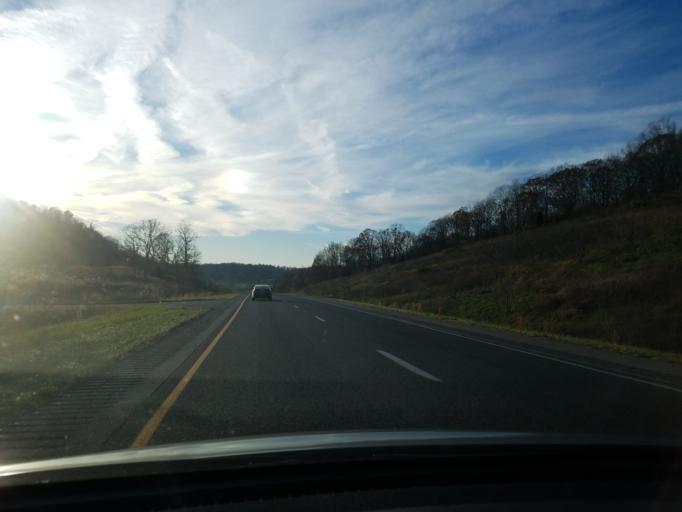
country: US
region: Indiana
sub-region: Dubois County
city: Ferdinand
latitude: 38.2123
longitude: -86.7651
